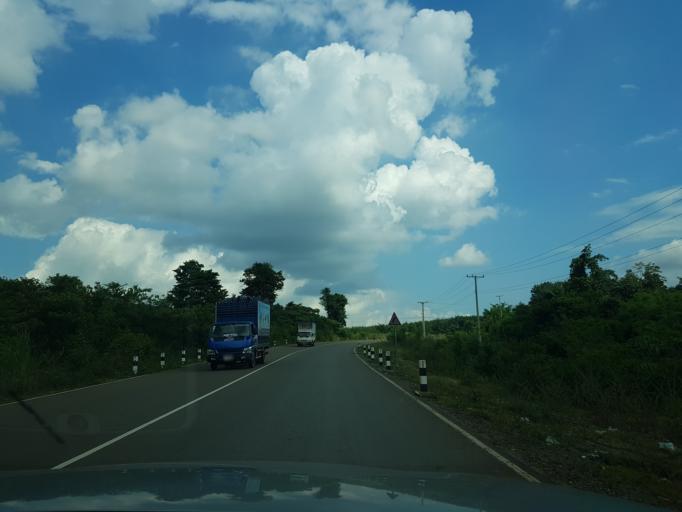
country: TH
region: Nong Khai
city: Sangkhom
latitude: 18.0376
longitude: 102.3625
